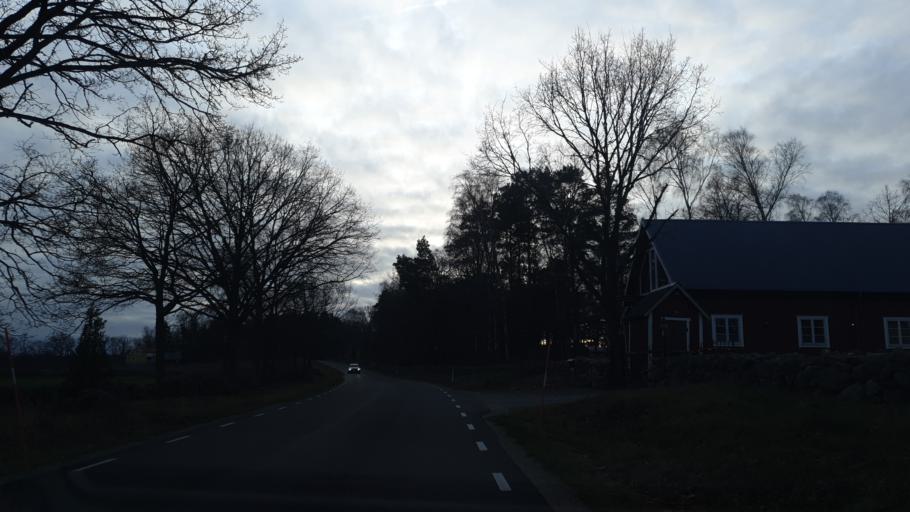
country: SE
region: Blekinge
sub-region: Karlskrona Kommun
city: Jaemjoe
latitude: 56.2274
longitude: 15.9924
